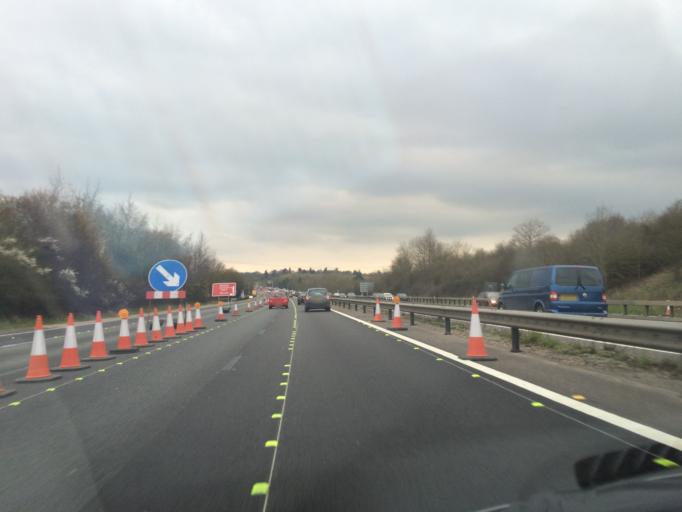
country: GB
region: England
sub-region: West Berkshire
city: Welford
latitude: 51.4508
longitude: -1.3982
